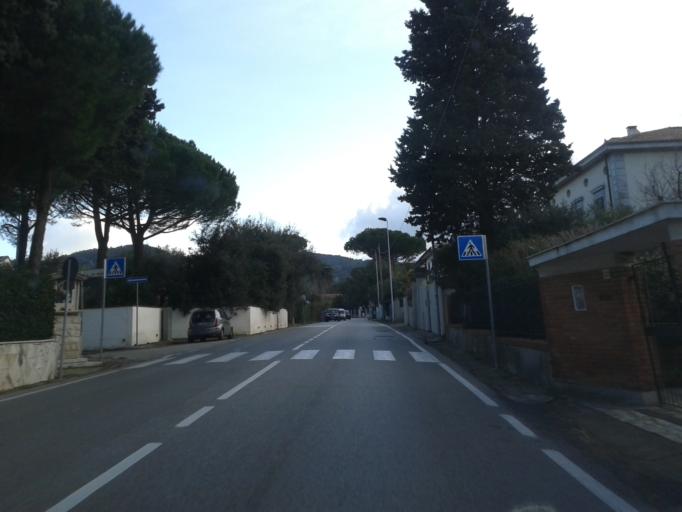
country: IT
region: Tuscany
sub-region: Provincia di Livorno
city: Livorno
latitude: 43.5046
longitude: 10.3381
